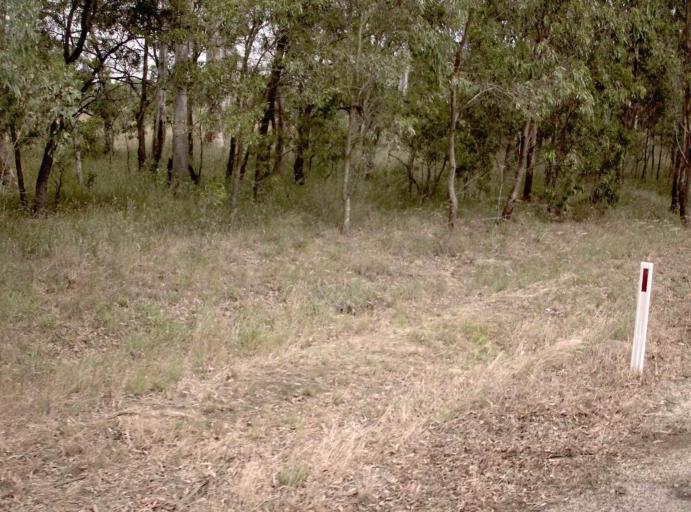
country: AU
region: Victoria
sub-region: Wellington
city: Sale
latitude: -37.8985
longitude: 147.0725
